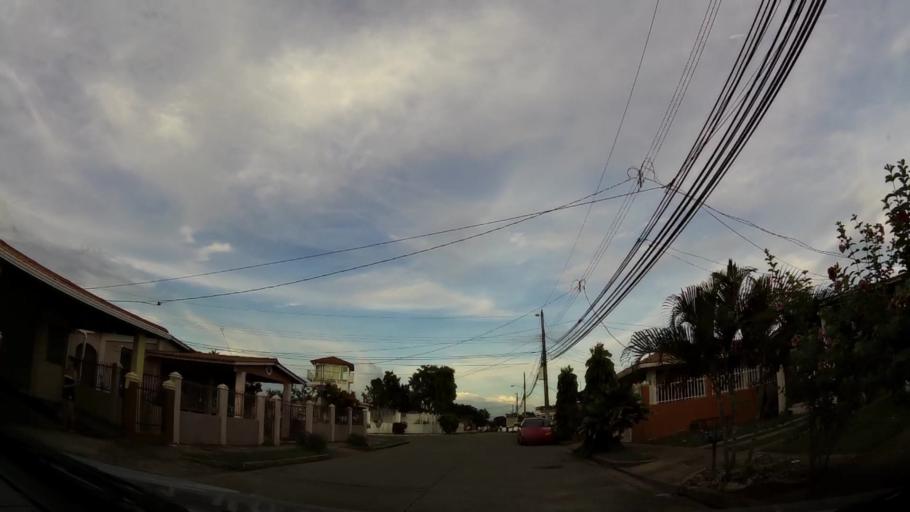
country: PA
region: Panama
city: La Chorrera
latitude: 8.8687
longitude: -79.7666
